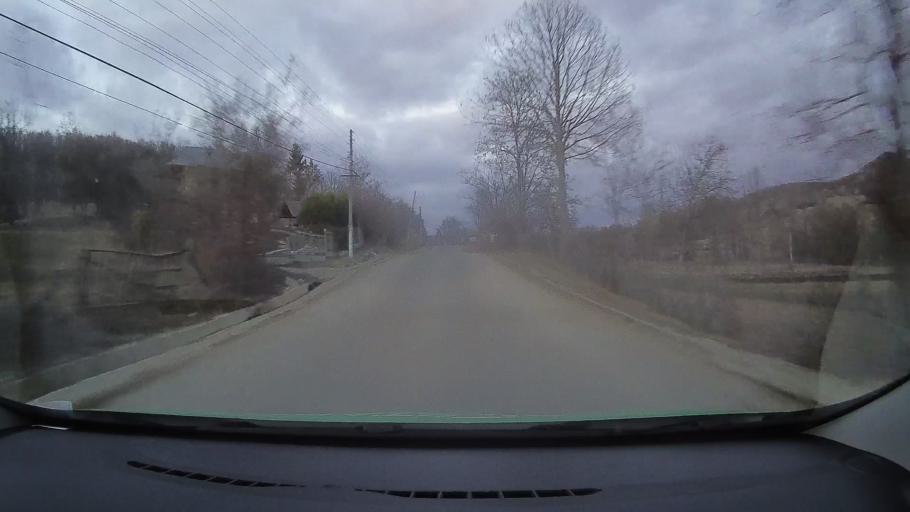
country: RO
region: Dambovita
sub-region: Comuna Visinesti
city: Visinesti
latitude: 45.0991
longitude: 25.5787
